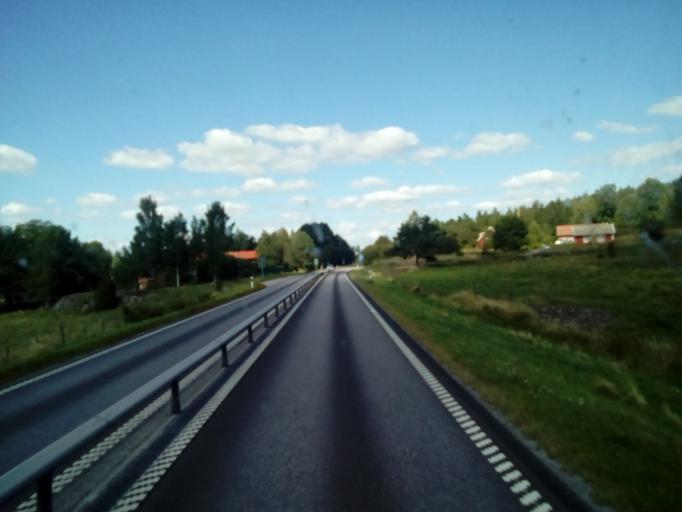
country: SE
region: OEstergoetland
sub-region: Linkopings Kommun
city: Malmslatt
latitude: 58.2997
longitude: 15.5640
